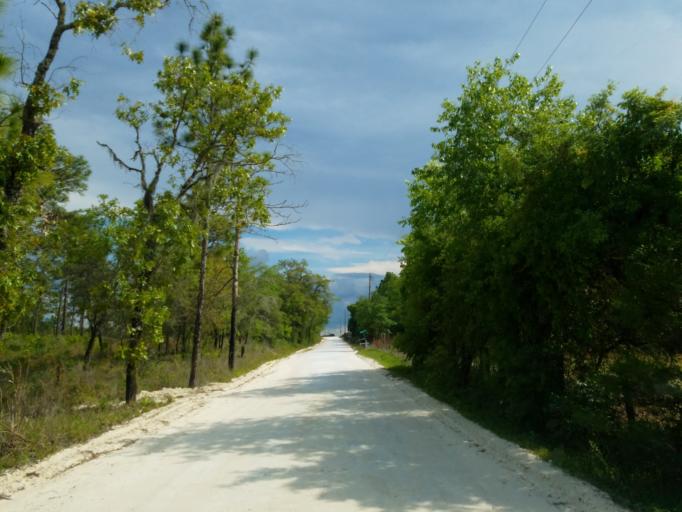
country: US
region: Florida
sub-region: Hernando County
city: Hill 'n Dale
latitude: 28.5378
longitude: -82.2759
